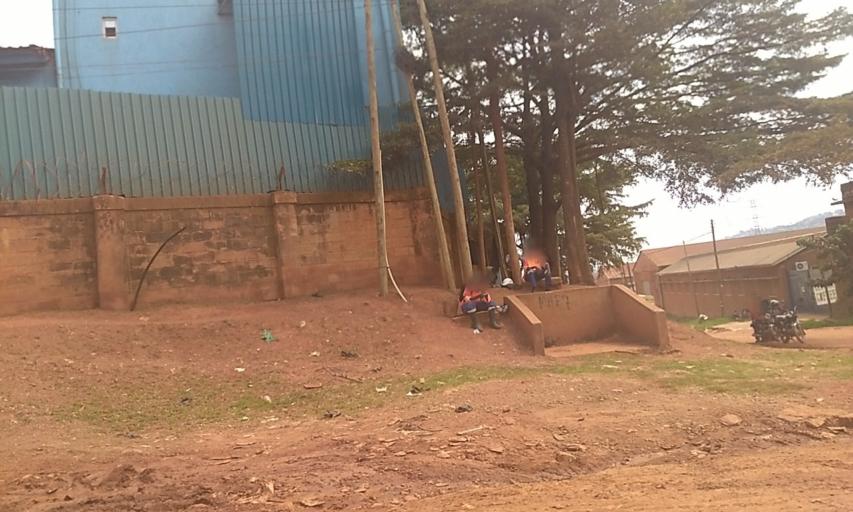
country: UG
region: Central Region
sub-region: Wakiso District
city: Kireka
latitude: 0.3376
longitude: 32.6200
